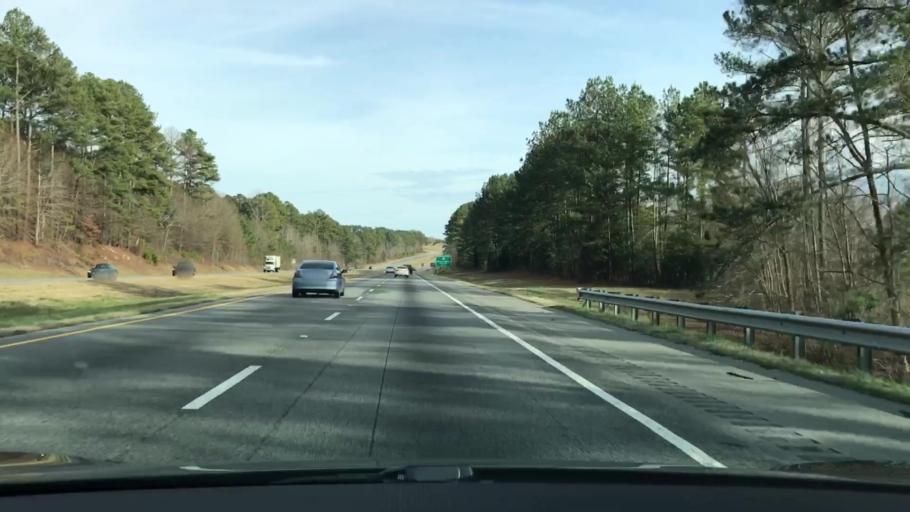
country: US
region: Georgia
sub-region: Walton County
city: Social Circle
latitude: 33.6111
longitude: -83.7152
